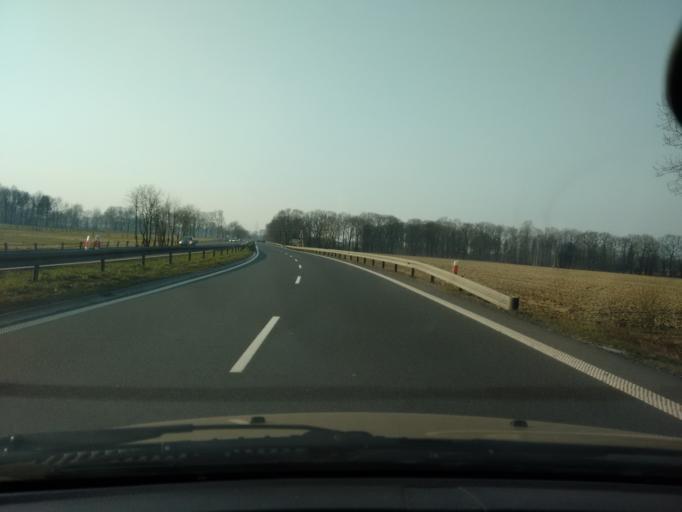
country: PL
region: Silesian Voivodeship
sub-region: Powiat cieszynski
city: Drogomysl
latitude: 49.8580
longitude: 18.7580
